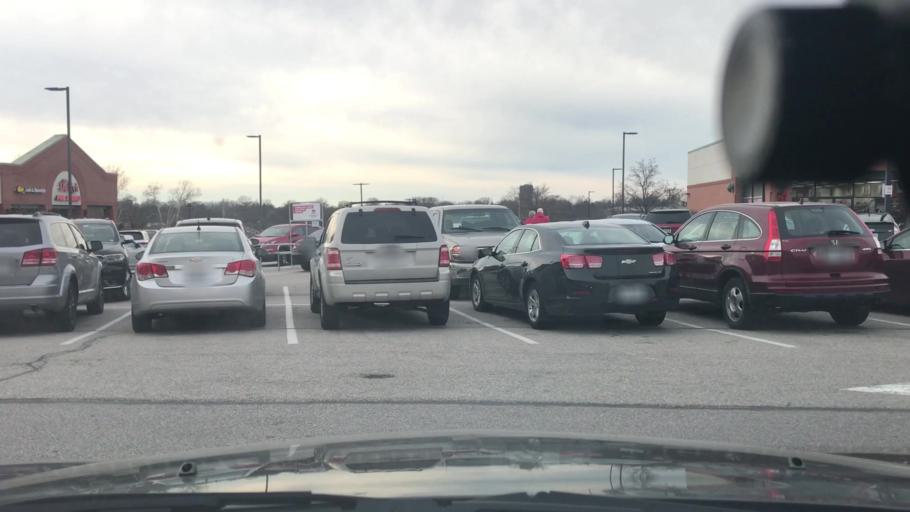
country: US
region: Missouri
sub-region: Saint Louis County
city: Richmond Heights
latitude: 38.6336
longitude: -90.3155
